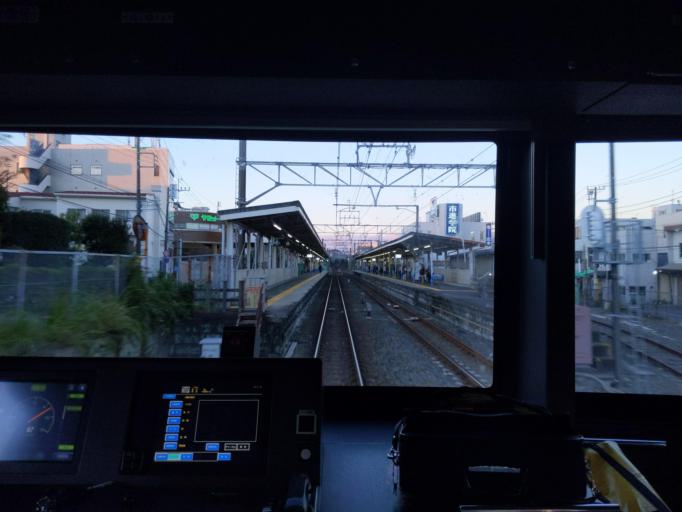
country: JP
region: Chiba
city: Funabashi
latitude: 35.7409
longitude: 139.9922
